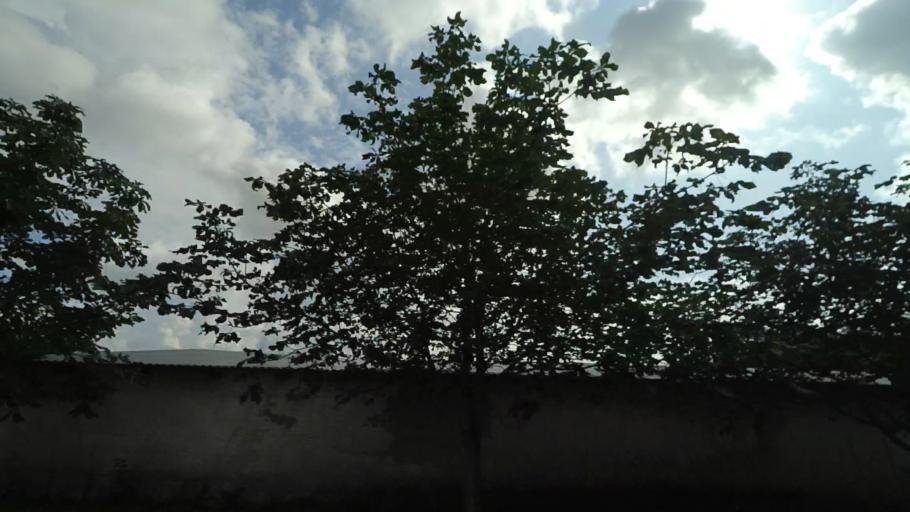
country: DK
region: Central Jutland
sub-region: Syddjurs Kommune
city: Ryomgard
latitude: 56.4823
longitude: 10.4847
